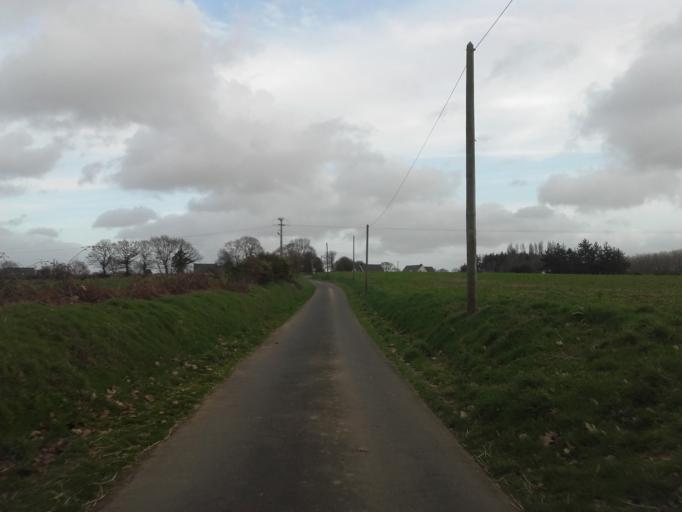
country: FR
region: Brittany
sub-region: Departement des Cotes-d'Armor
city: Lanvollon
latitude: 48.6535
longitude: -2.9885
